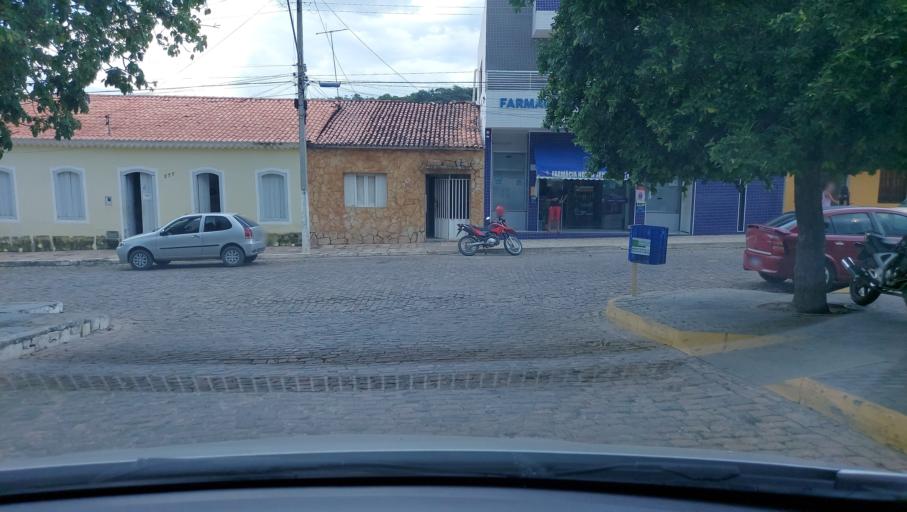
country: BR
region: Bahia
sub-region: Oliveira Dos Brejinhos
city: Beira Rio
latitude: -11.9987
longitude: -42.6264
